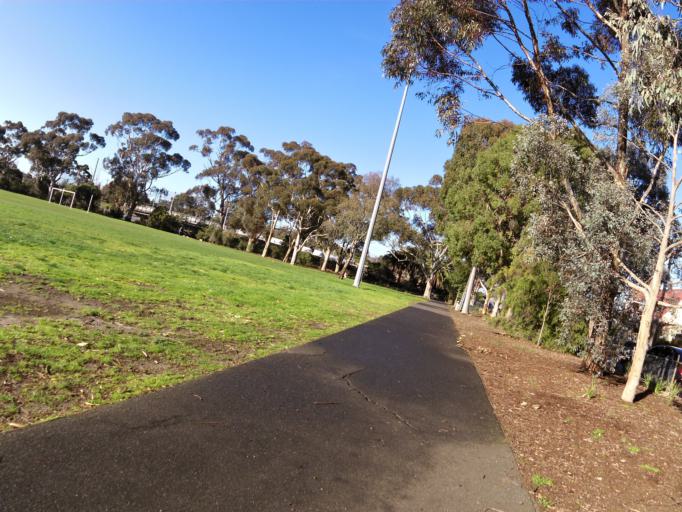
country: AU
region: Victoria
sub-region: Yarra
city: Richmond
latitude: -37.8261
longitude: 145.0134
